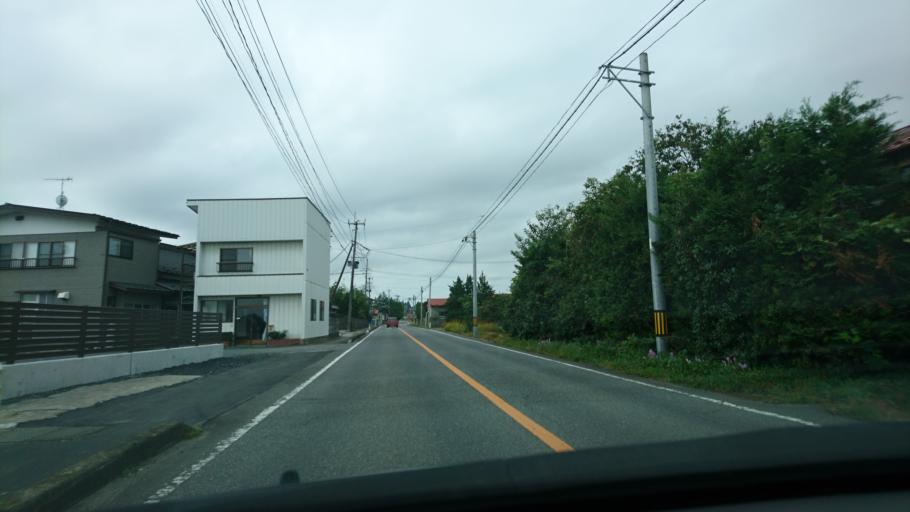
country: JP
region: Iwate
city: Ichinoseki
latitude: 38.7473
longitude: 141.0509
